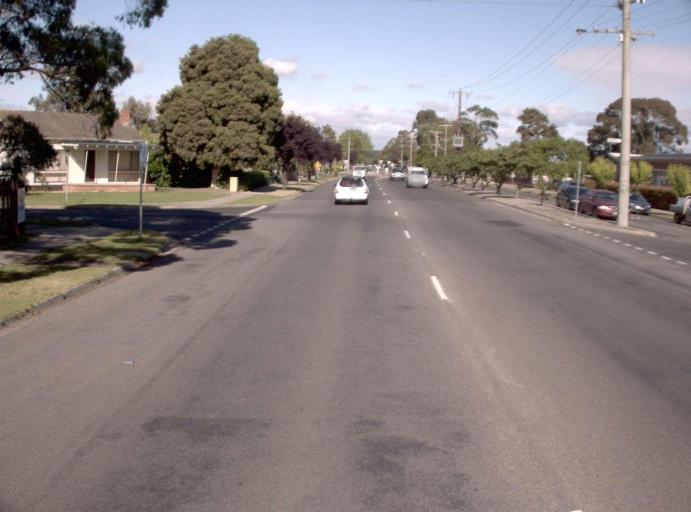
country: AU
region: Victoria
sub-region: Latrobe
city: Traralgon
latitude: -38.1915
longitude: 146.5171
